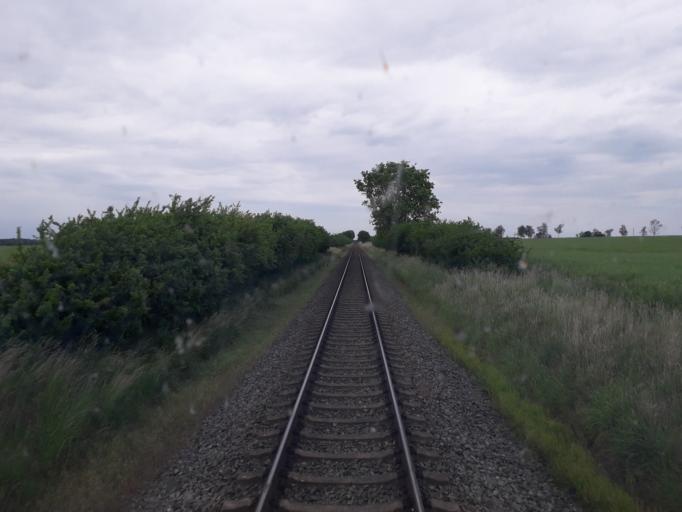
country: DE
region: Brandenburg
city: Neuruppin
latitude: 52.8902
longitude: 12.8507
